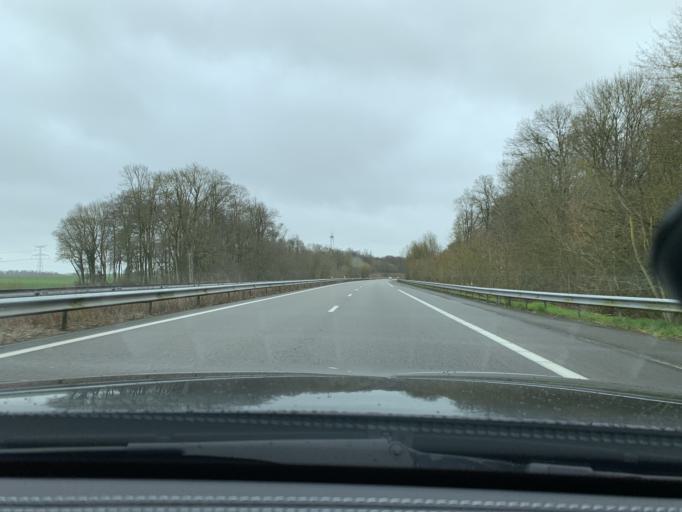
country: FR
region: Picardie
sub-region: Departement de l'Oise
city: Breteuil
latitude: 49.6572
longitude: 2.2132
